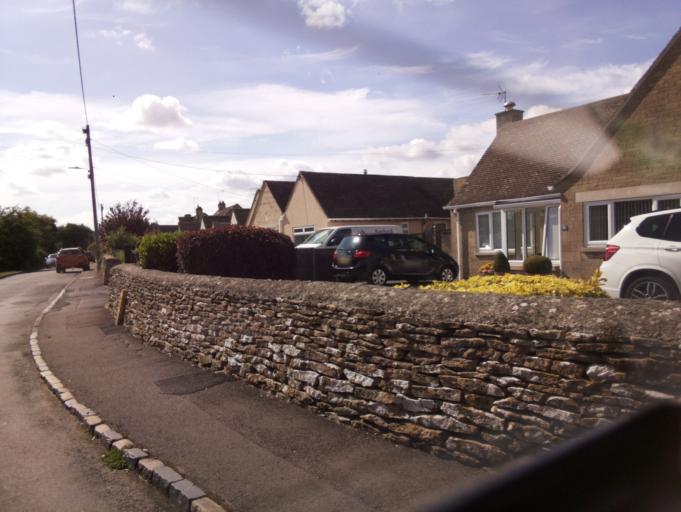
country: GB
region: England
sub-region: Gloucestershire
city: Tetbury
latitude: 51.6320
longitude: -2.1673
